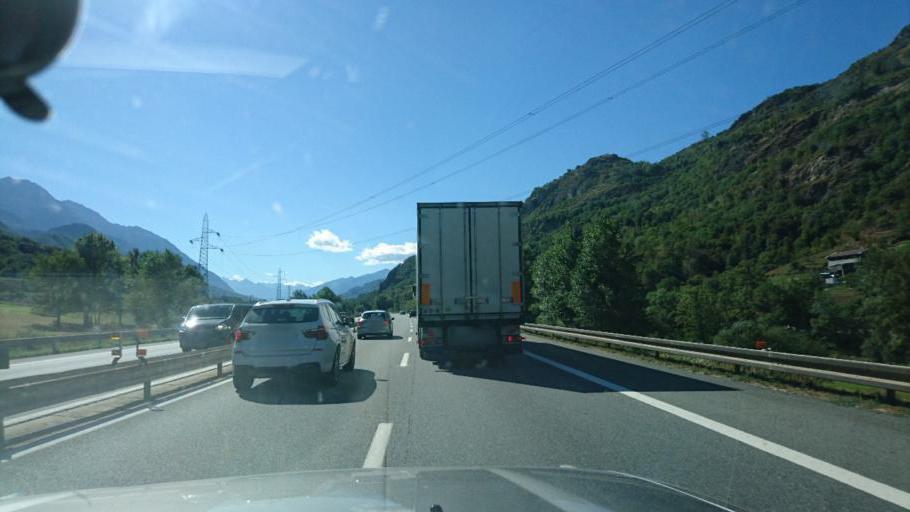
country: IT
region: Aosta Valley
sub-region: Valle d'Aosta
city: Pontey
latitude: 45.7443
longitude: 7.5769
